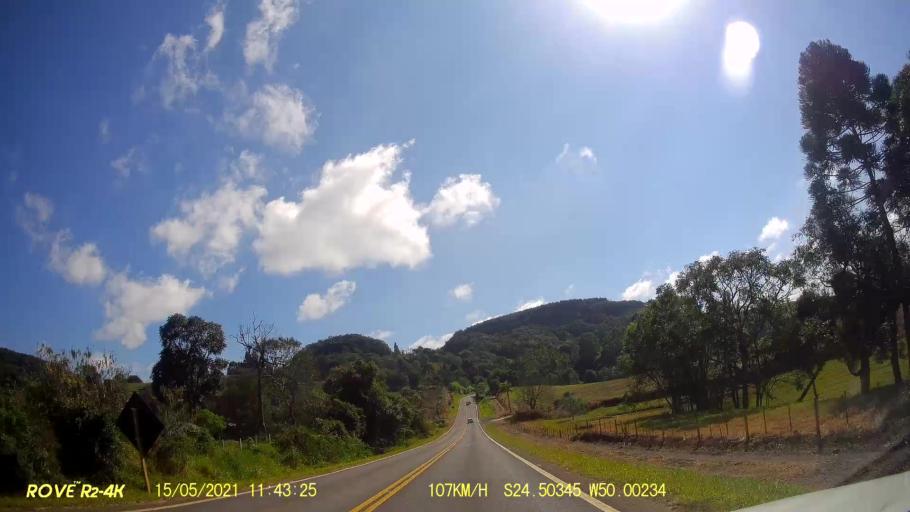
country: BR
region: Parana
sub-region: Pirai Do Sul
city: Pirai do Sul
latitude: -24.5035
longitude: -50.0022
